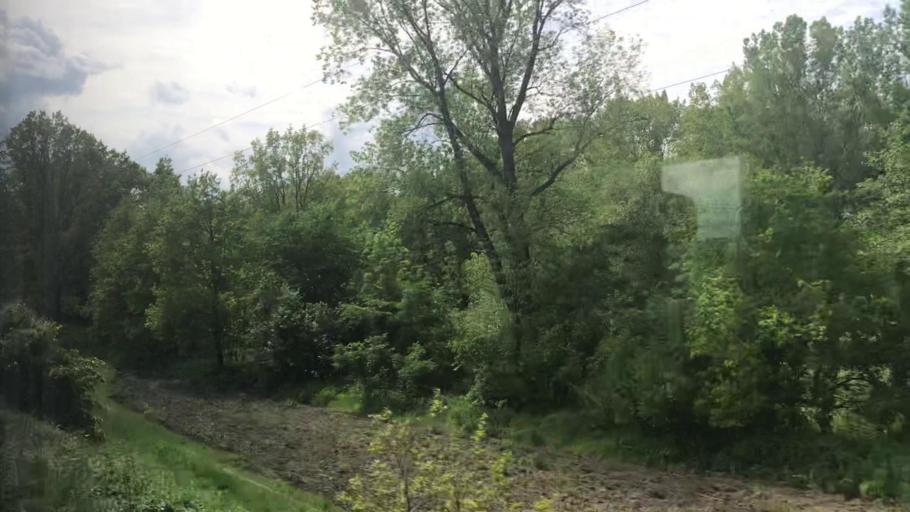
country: PL
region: Lower Silesian Voivodeship
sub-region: Powiat swidnicki
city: Stanowice
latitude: 50.8878
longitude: 16.3914
